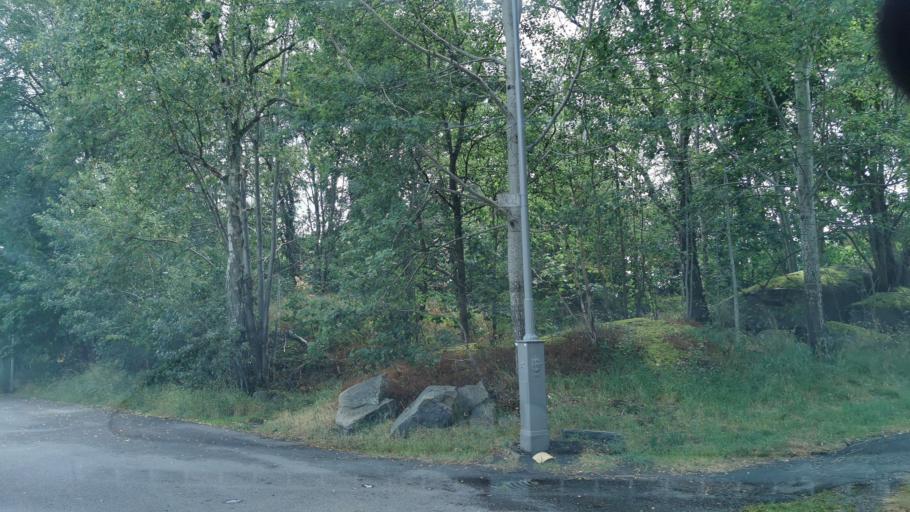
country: SE
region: Vaestra Goetaland
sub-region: Goteborg
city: Goeteborg
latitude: 57.6778
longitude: 11.9804
